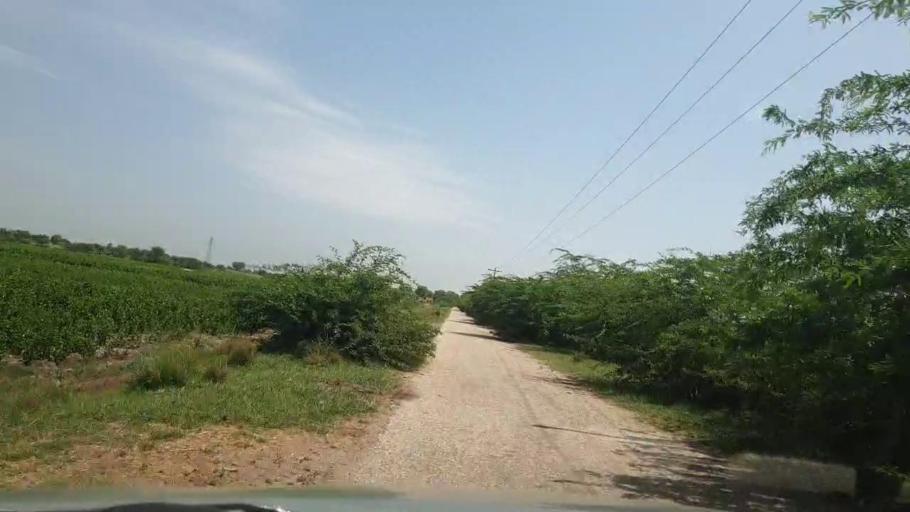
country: PK
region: Sindh
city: Bozdar
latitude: 27.1045
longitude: 68.9793
